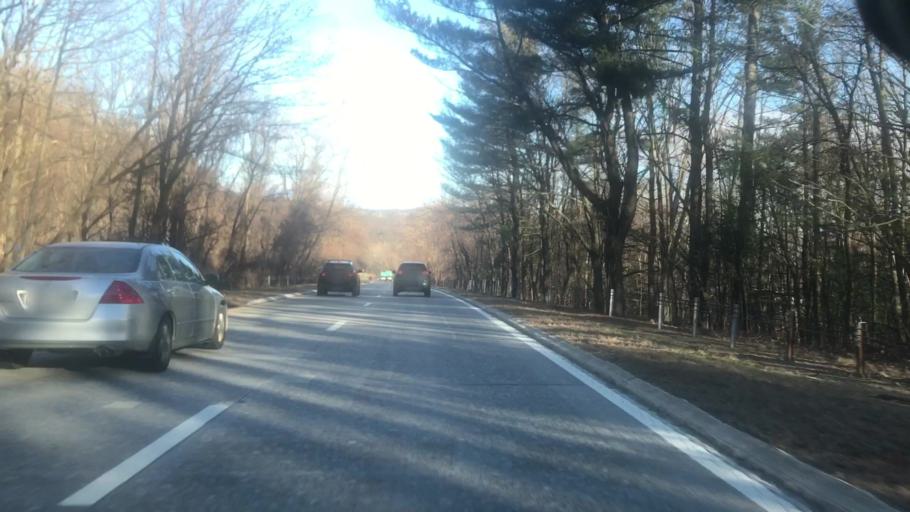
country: US
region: New York
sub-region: Rockland County
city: Thiells
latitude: 41.2124
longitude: -74.0323
